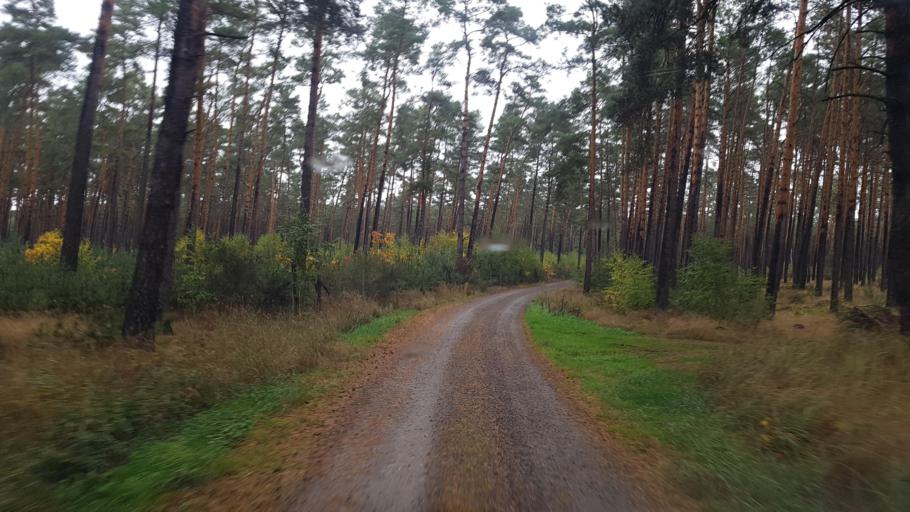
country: DE
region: Brandenburg
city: Schlieben
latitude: 51.7771
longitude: 13.3475
